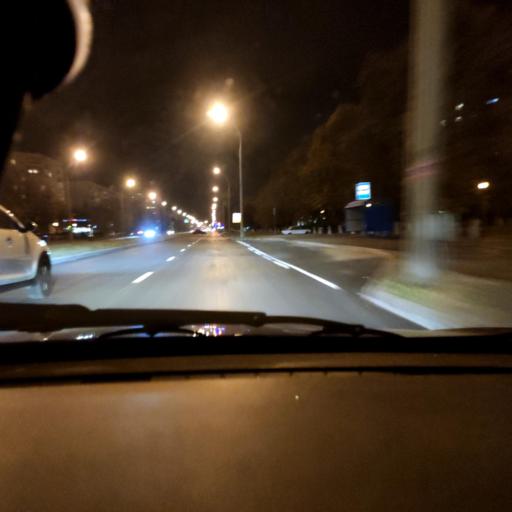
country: RU
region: Samara
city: Tol'yatti
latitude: 53.5359
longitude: 49.3293
